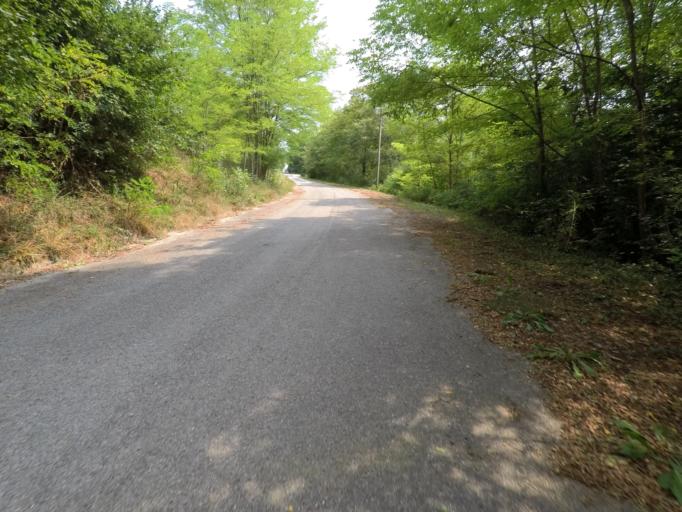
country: IT
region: Friuli Venezia Giulia
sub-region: Provincia di Pordenone
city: Caneva
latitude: 46.0036
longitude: 12.4767
